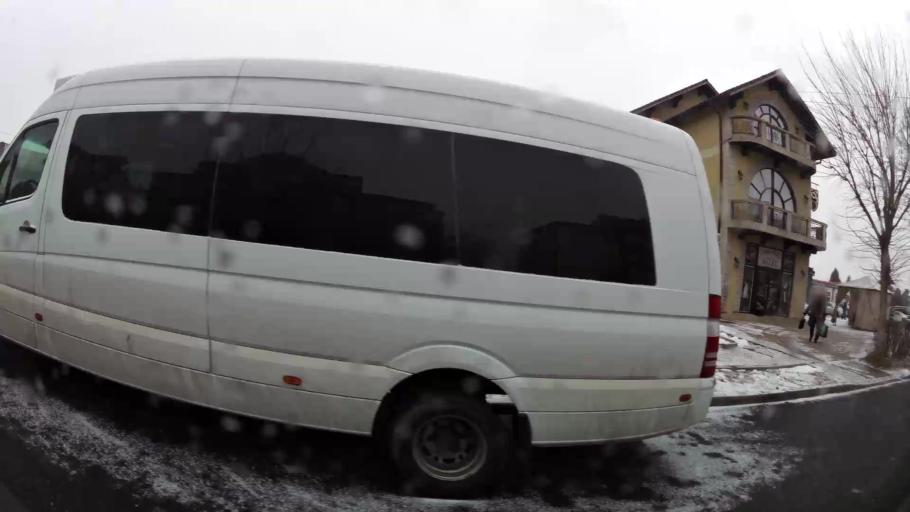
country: RO
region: Dambovita
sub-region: Municipiul Targoviste
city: Targoviste
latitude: 44.9305
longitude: 25.4394
